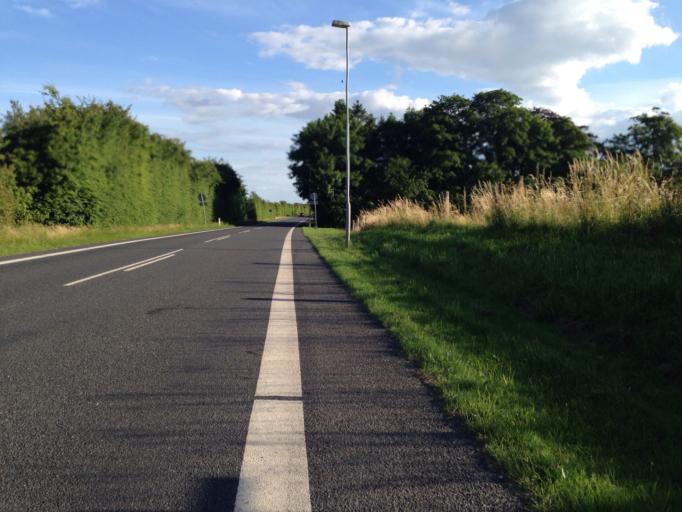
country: DK
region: South Denmark
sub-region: Middelfart Kommune
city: Norre Aby
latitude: 55.4802
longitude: 9.9012
